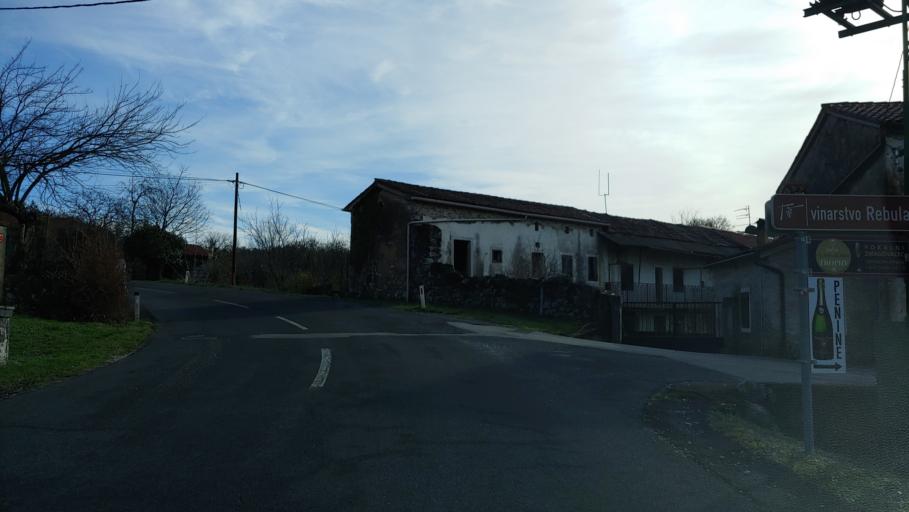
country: IT
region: Friuli Venezia Giulia
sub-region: Provincia di Trieste
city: Sistiana-Visogliano
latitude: 45.8121
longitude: 13.6429
